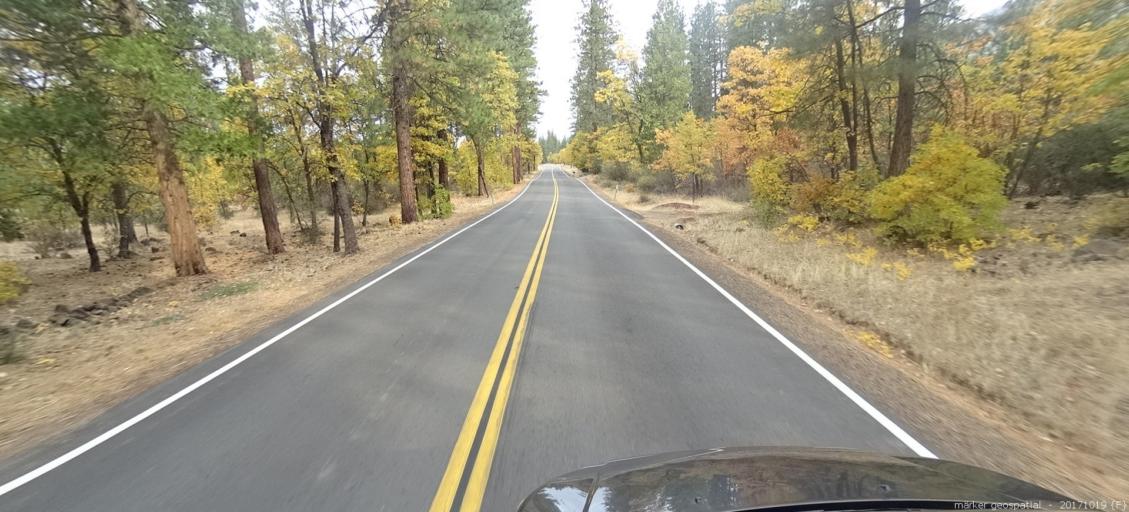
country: US
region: California
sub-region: Shasta County
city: Burney
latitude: 41.1644
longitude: -121.3579
